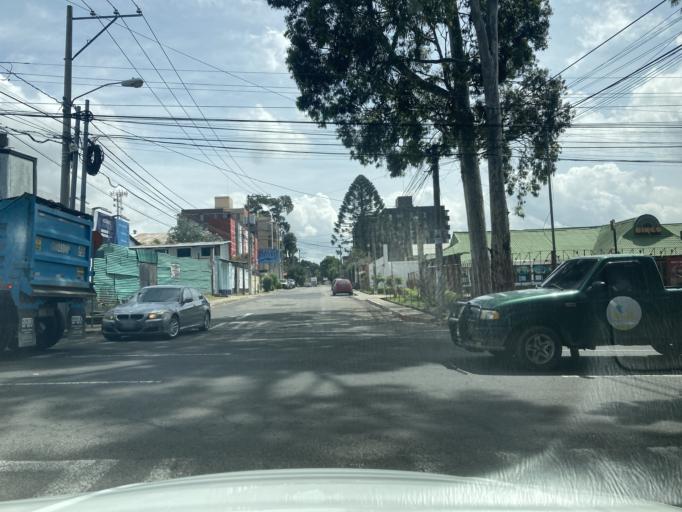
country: GT
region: Guatemala
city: Mixco
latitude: 14.5934
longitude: -90.5634
